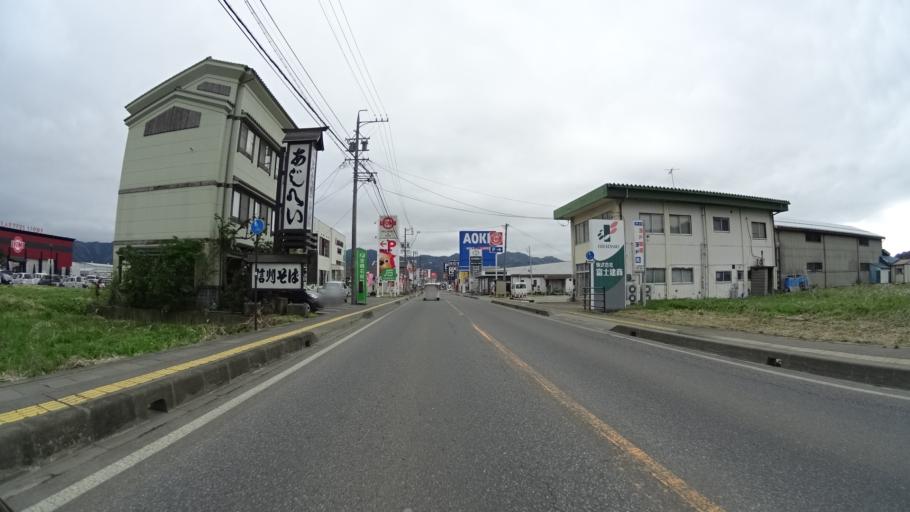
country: JP
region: Nagano
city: Nakano
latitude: 36.7488
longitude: 138.3508
